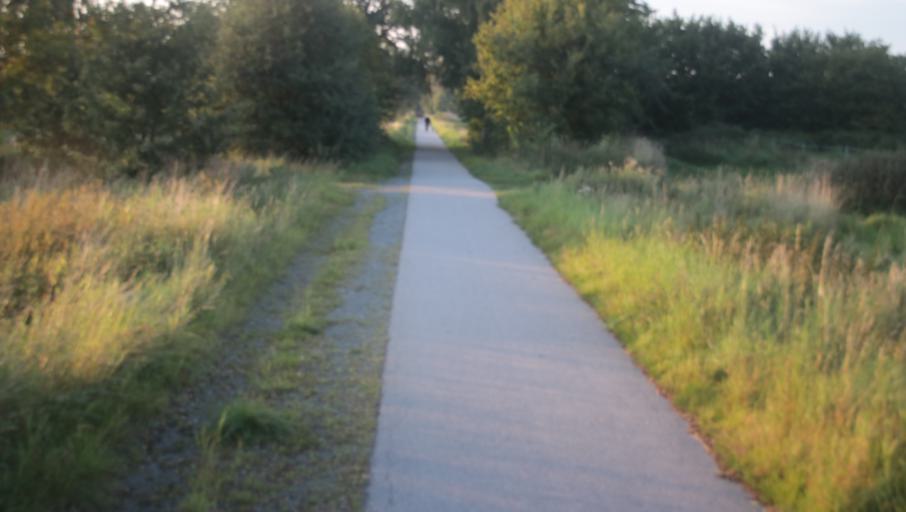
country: SE
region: Blekinge
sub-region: Karlshamns Kommun
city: Karlshamn
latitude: 56.2145
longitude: 14.8255
